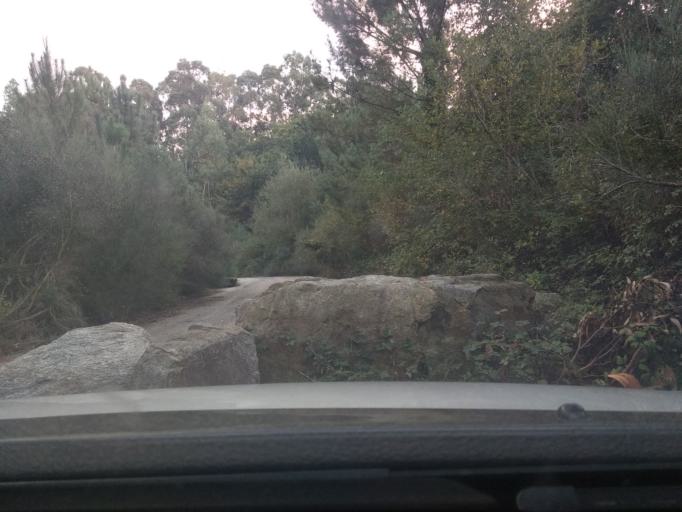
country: ES
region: Galicia
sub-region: Provincia de Pontevedra
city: Moana
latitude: 42.3017
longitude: -8.6960
